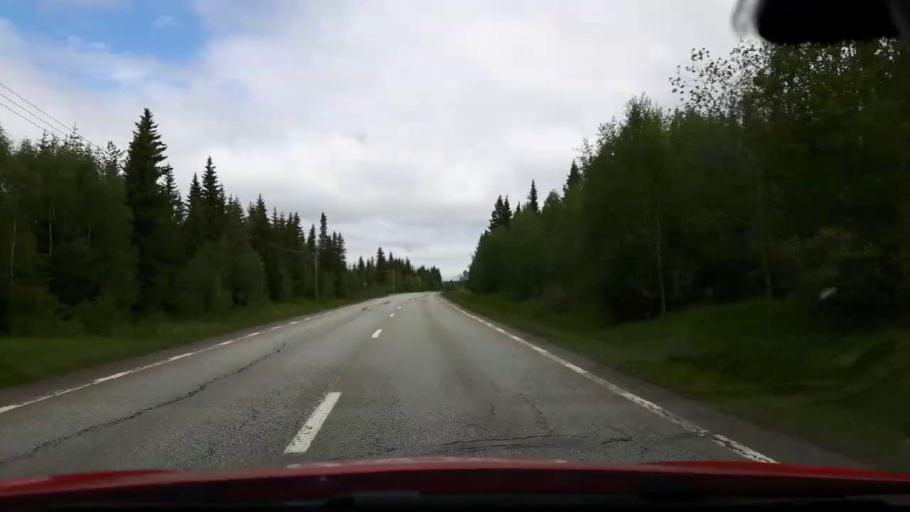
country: SE
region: Jaemtland
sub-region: Krokoms Kommun
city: Krokom
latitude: 63.4666
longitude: 14.4958
